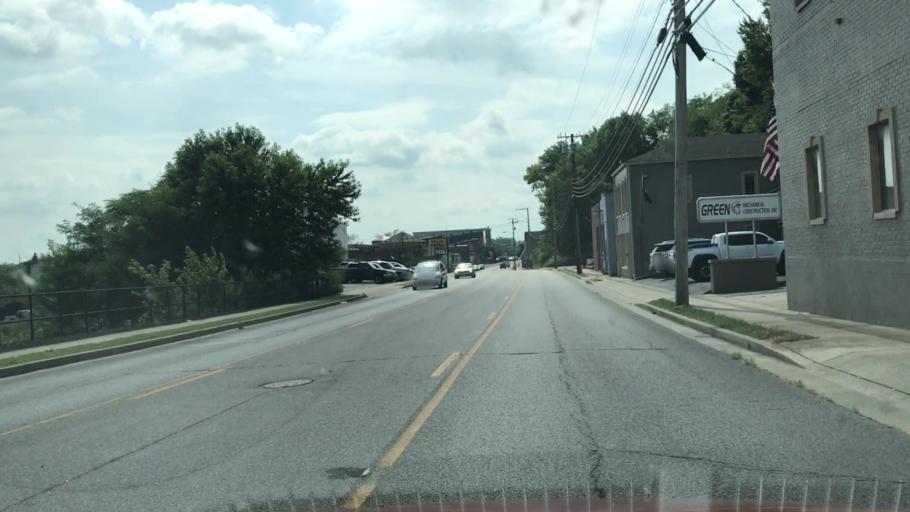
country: US
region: Kentucky
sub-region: Barren County
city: Glasgow
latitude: 36.9975
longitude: -85.9161
